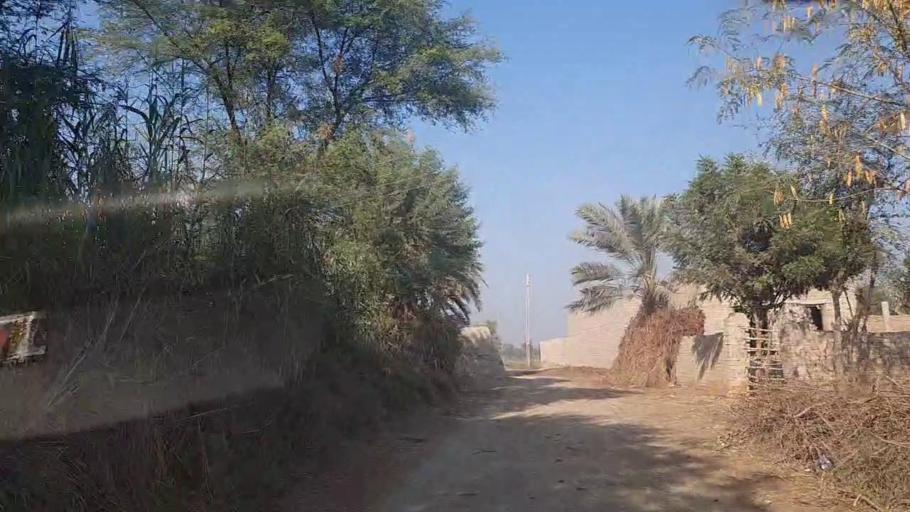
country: PK
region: Sindh
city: Gambat
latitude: 27.3644
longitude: 68.4755
